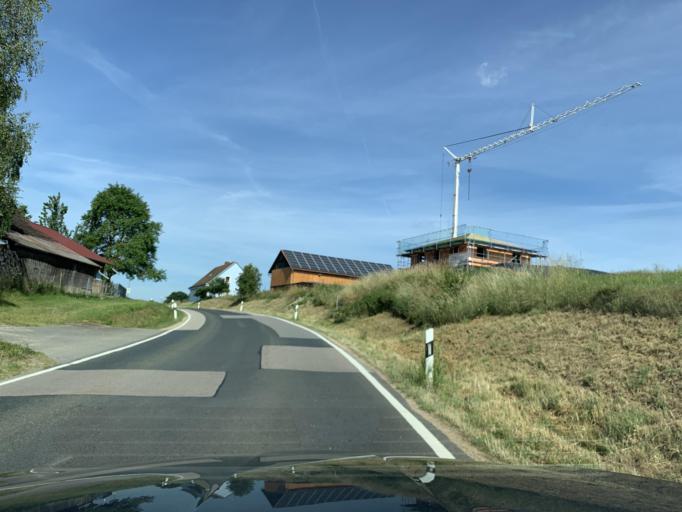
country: DE
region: Bavaria
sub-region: Upper Palatinate
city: Schwarzhofen
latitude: 49.3948
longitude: 12.3270
